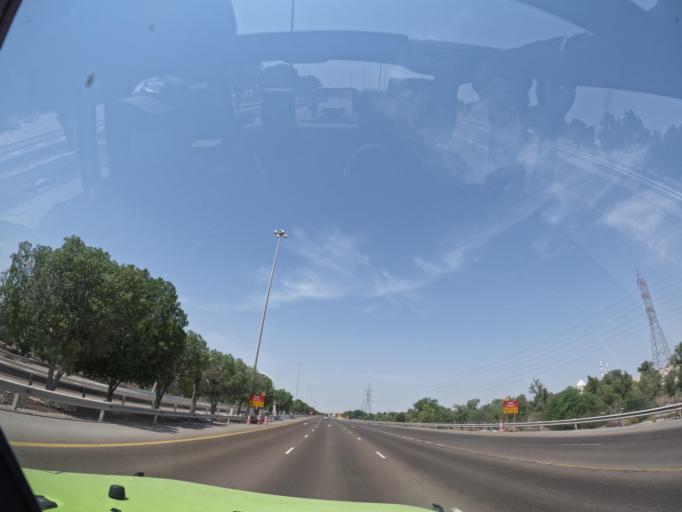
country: AE
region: Abu Dhabi
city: Abu Dhabi
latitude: 24.2532
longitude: 54.7050
